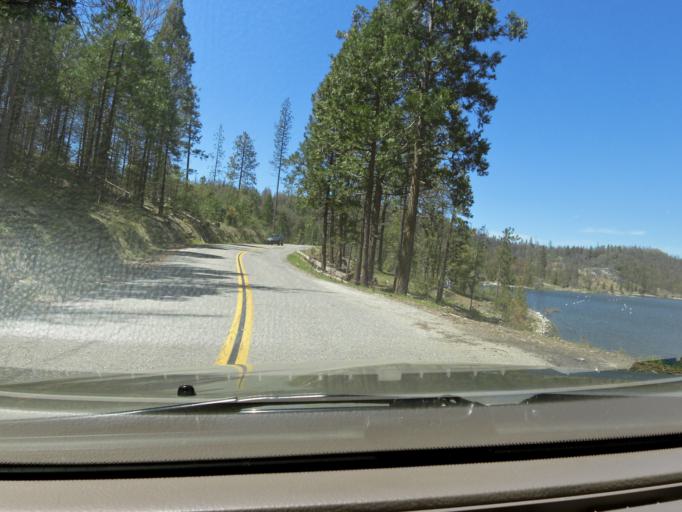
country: US
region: California
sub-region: Madera County
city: Oakhurst
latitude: 37.3143
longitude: -119.5671
